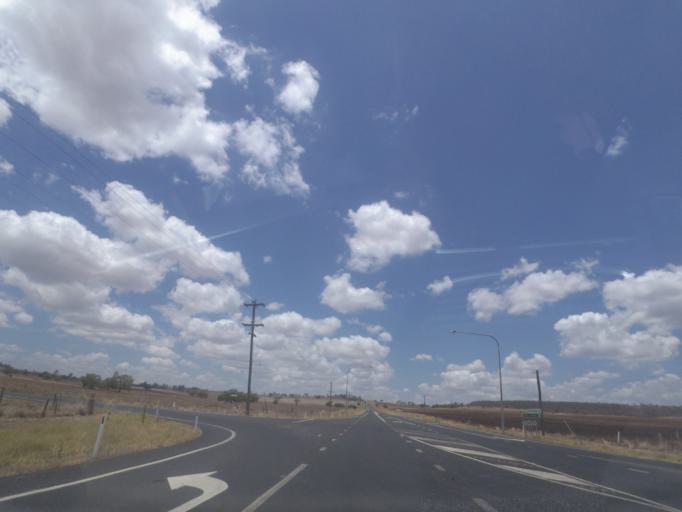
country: AU
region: Queensland
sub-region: Toowoomba
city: Top Camp
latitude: -27.7176
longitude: 151.9115
